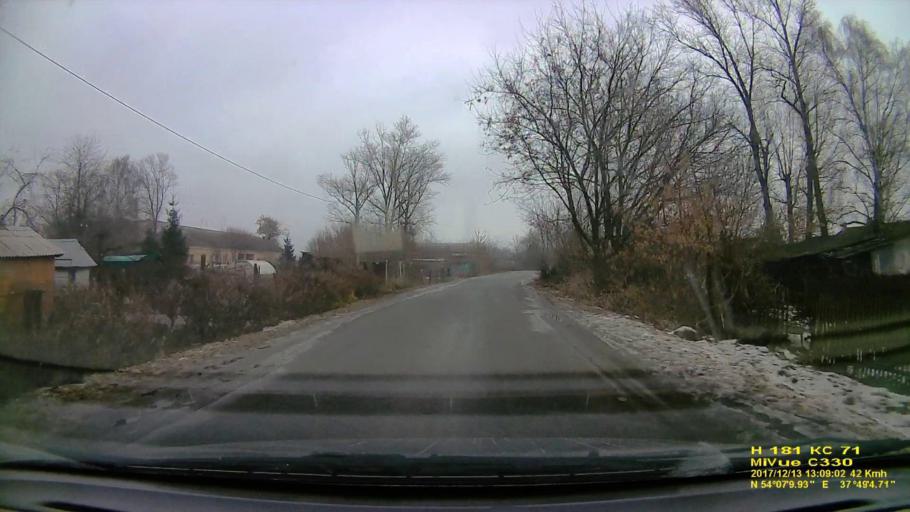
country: RU
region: Tula
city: Bolokhovo
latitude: 54.1194
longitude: 37.8180
